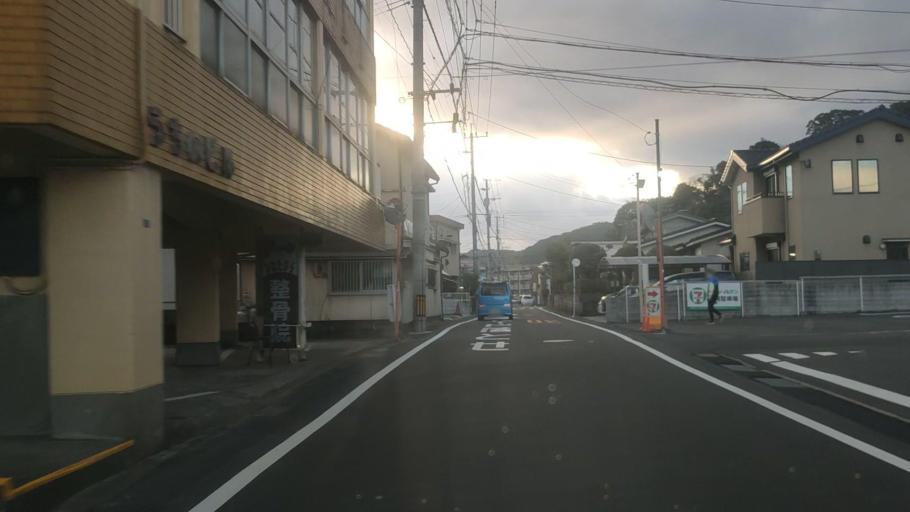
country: JP
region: Kagoshima
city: Kagoshima-shi
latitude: 31.6180
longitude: 130.5348
